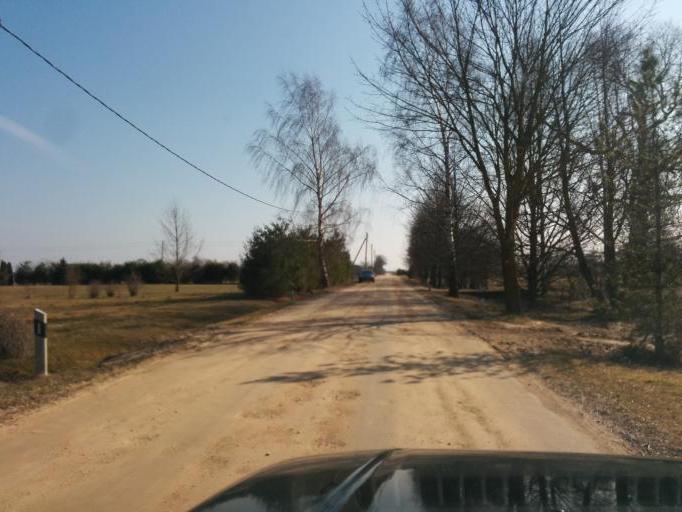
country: LV
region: Ozolnieku
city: Ozolnieki
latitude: 56.6400
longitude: 23.7792
